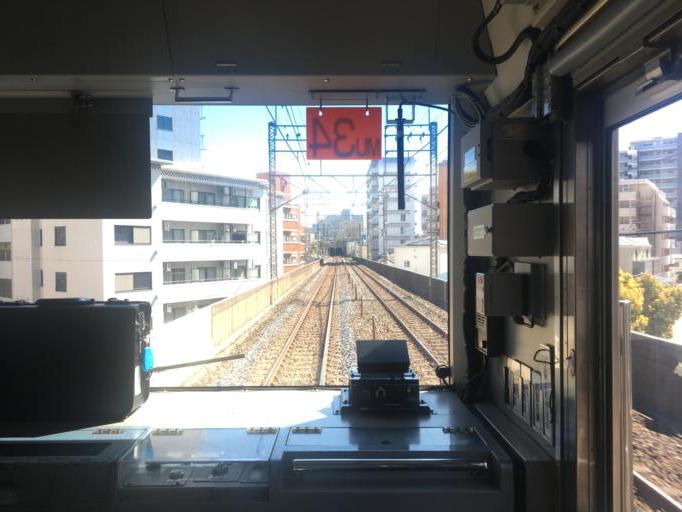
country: JP
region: Saitama
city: Yono
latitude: 35.8459
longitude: 139.6518
